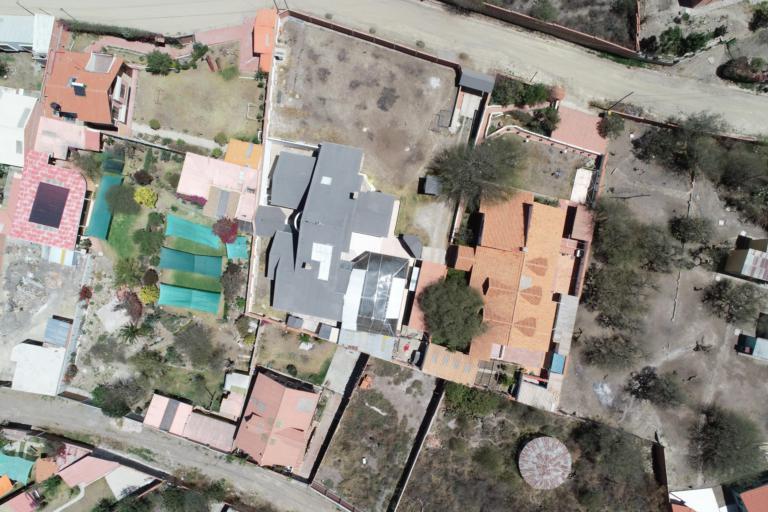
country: BO
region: La Paz
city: La Paz
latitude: -16.6448
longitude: -68.0436
